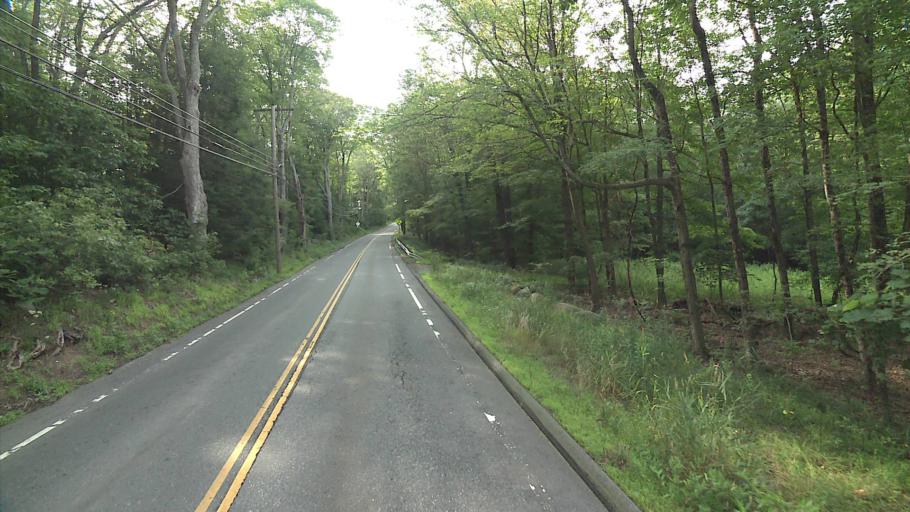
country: US
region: Massachusetts
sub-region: Worcester County
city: Southbridge
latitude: 41.9793
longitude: -72.0760
